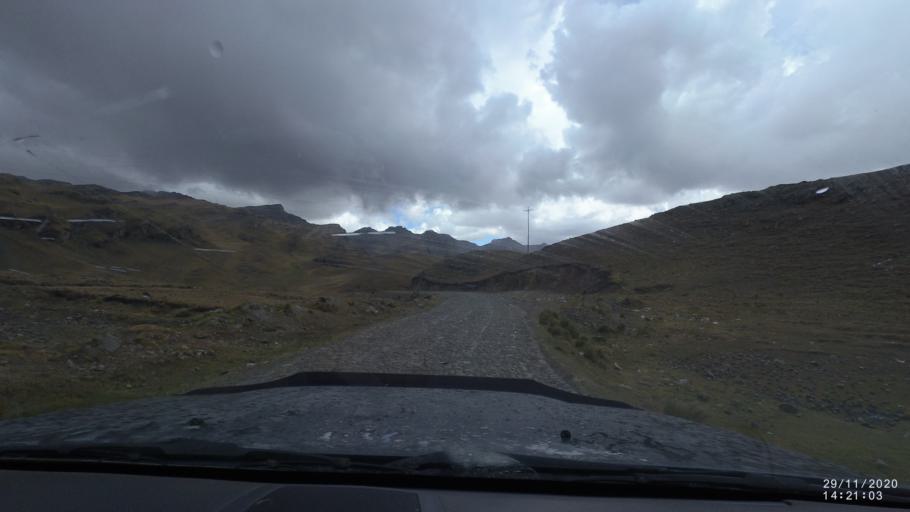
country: BO
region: Cochabamba
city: Sipe Sipe
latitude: -17.2505
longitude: -66.3899
